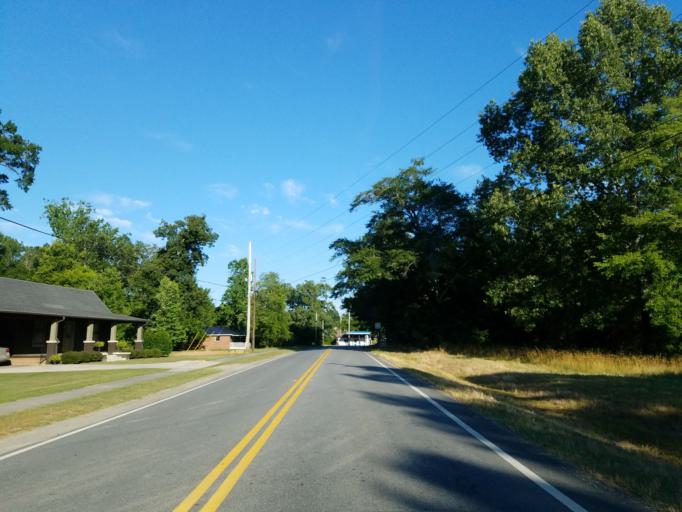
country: US
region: Georgia
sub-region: Gordon County
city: Calhoun
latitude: 34.5590
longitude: -85.0155
